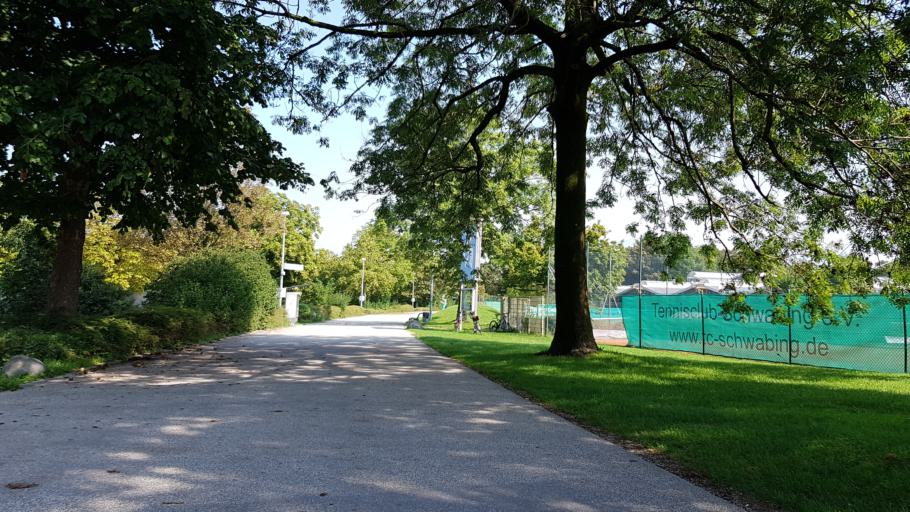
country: DE
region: Bavaria
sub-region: Upper Bavaria
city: Munich
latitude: 48.1728
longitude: 11.5422
